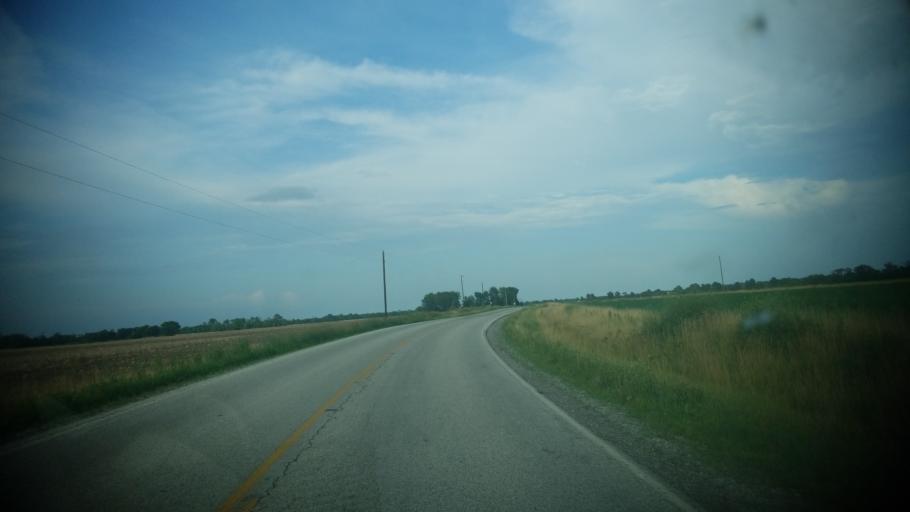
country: US
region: Illinois
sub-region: Clay County
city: Flora
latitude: 38.5174
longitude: -88.4824
